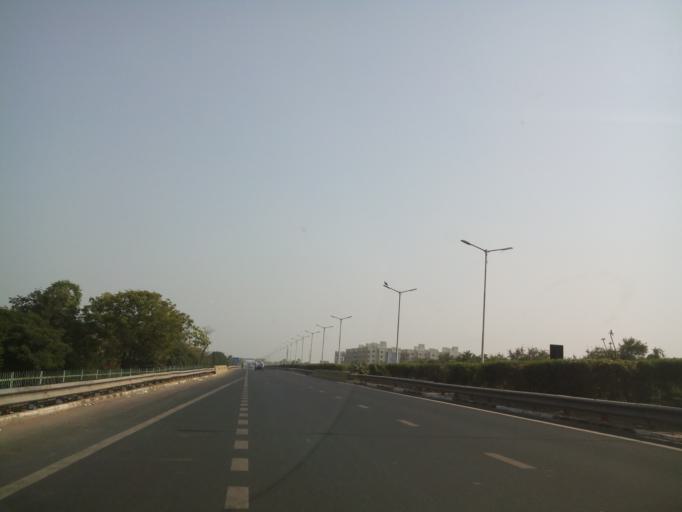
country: IN
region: Gujarat
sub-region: Ahmadabad
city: Ahmedabad
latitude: 22.9867
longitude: 72.6316
